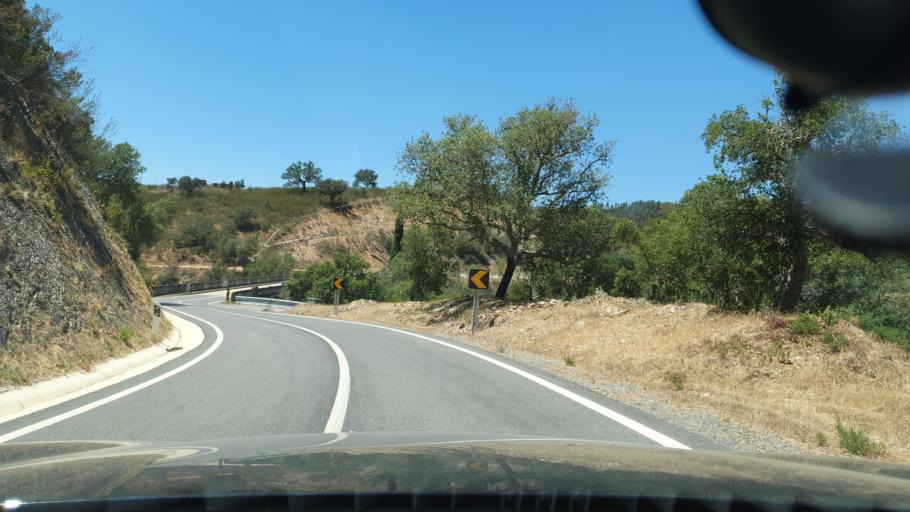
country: PT
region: Beja
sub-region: Odemira
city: Odemira
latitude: 37.5383
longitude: -8.4835
